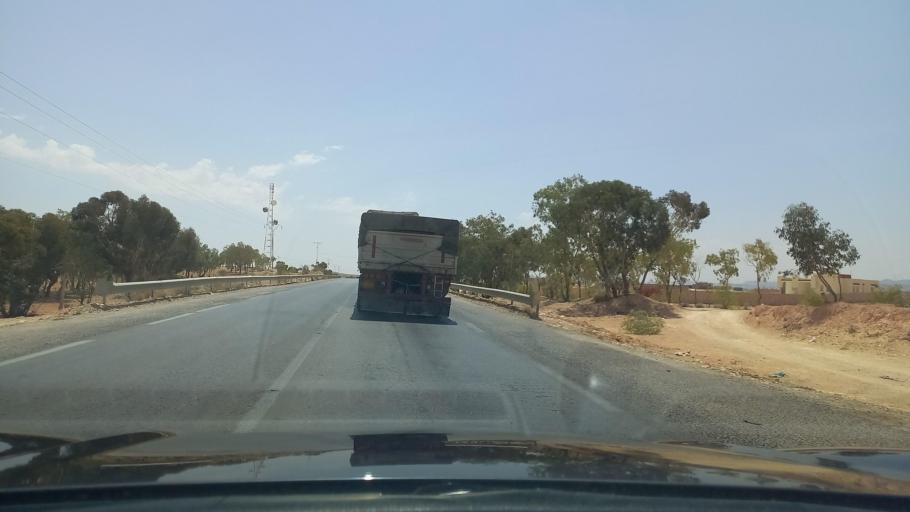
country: TN
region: Madanin
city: Medenine
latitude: 33.5717
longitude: 10.3171
